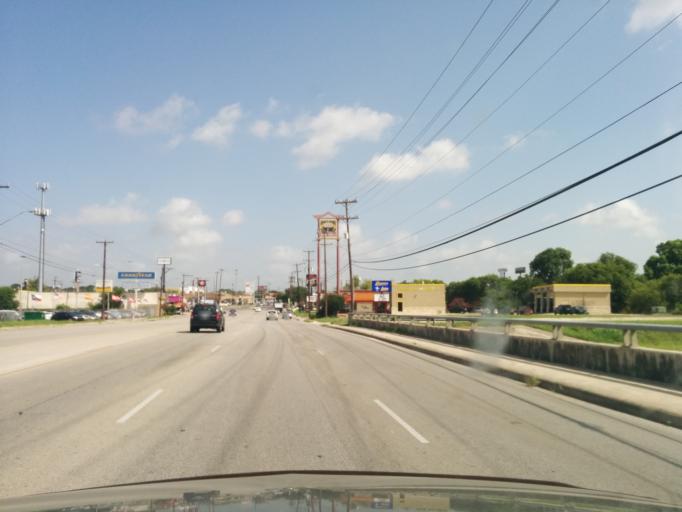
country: US
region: Texas
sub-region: Bexar County
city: Leon Valley
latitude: 29.5213
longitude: -98.5981
